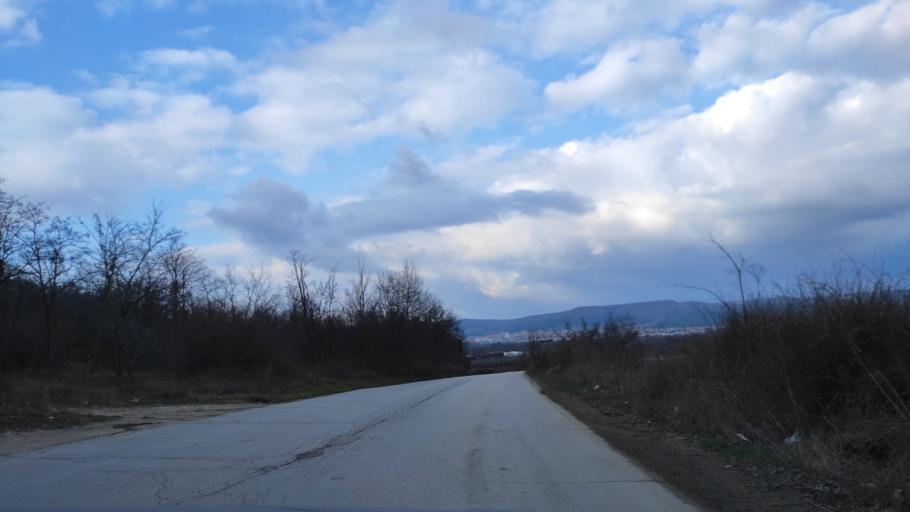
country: BG
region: Varna
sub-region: Obshtina Aksakovo
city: Aksakovo
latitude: 43.2270
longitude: 27.8052
